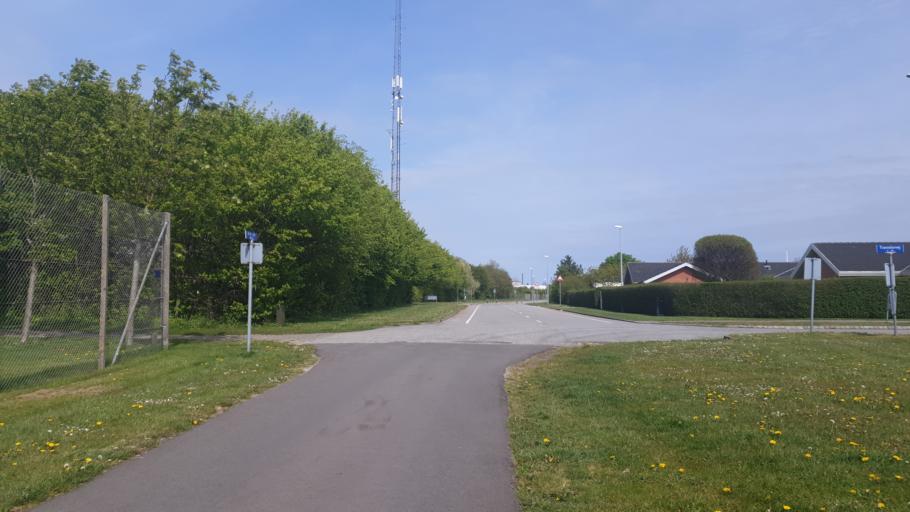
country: DK
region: Central Jutland
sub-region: Hedensted Kommune
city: Hedensted
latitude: 55.7935
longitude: 9.6926
